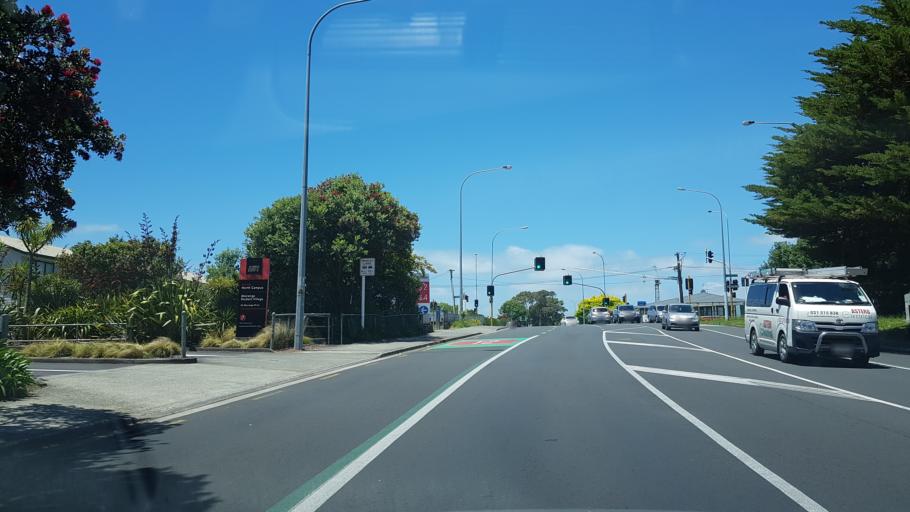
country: NZ
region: Auckland
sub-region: Auckland
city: North Shore
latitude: -36.7957
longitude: 174.7535
